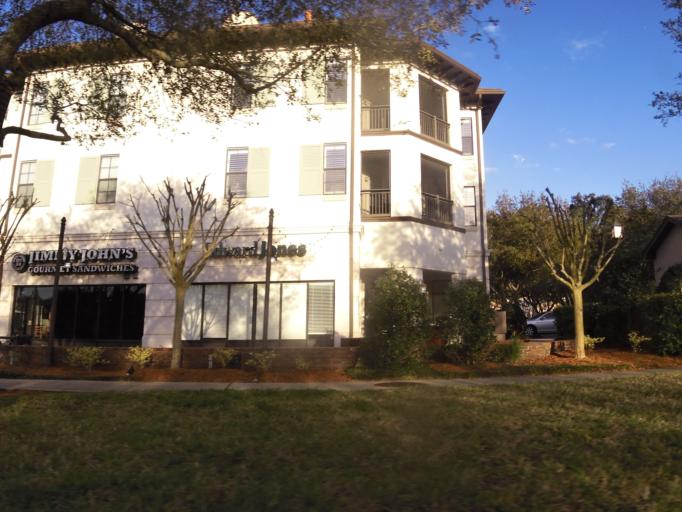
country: US
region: Florida
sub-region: Duval County
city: Jacksonville
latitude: 30.2573
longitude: -81.5541
